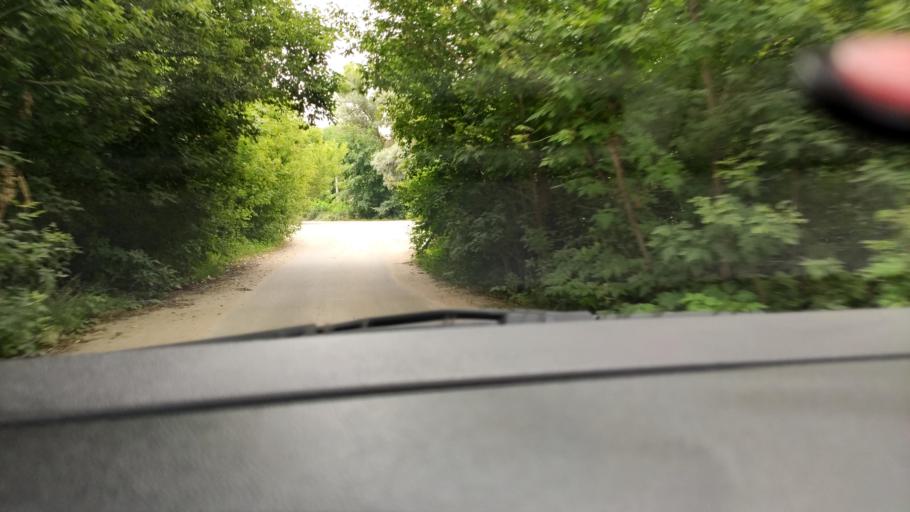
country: RU
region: Voronezj
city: Ramon'
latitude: 51.8941
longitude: 39.3516
